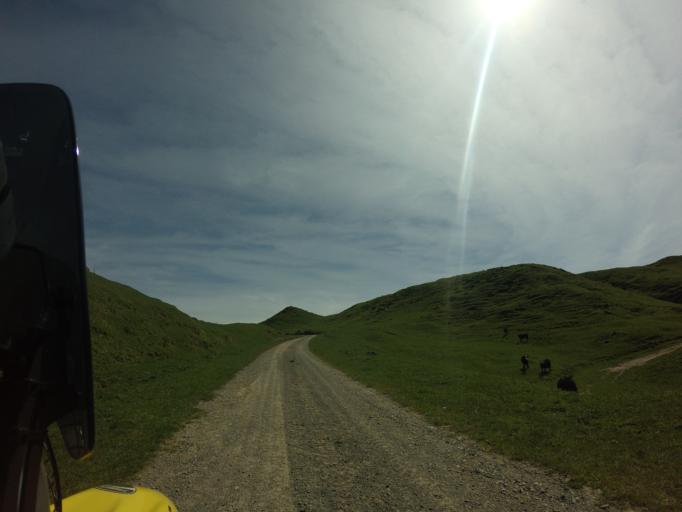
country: NZ
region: Bay of Plenty
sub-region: Opotiki District
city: Opotiki
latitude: -38.4528
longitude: 177.3652
